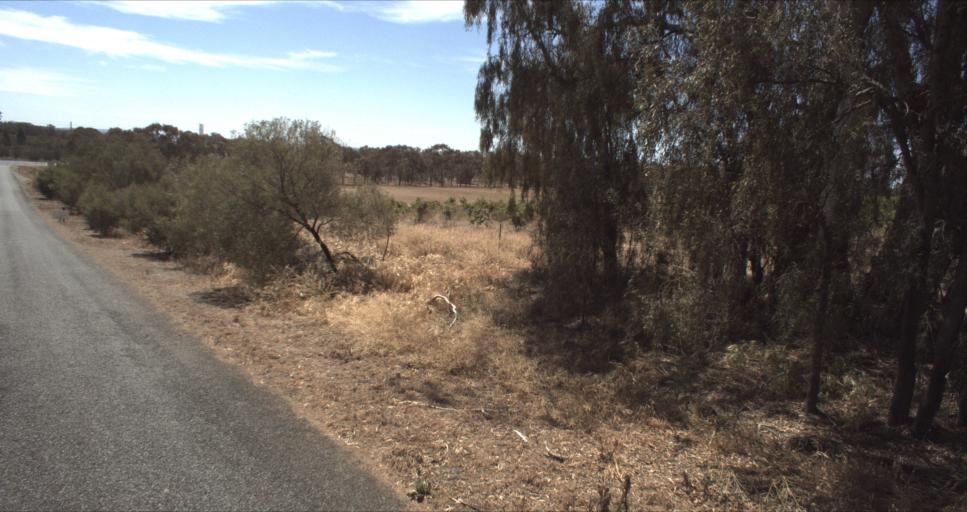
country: AU
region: New South Wales
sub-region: Leeton
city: Leeton
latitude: -34.6667
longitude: 146.4469
